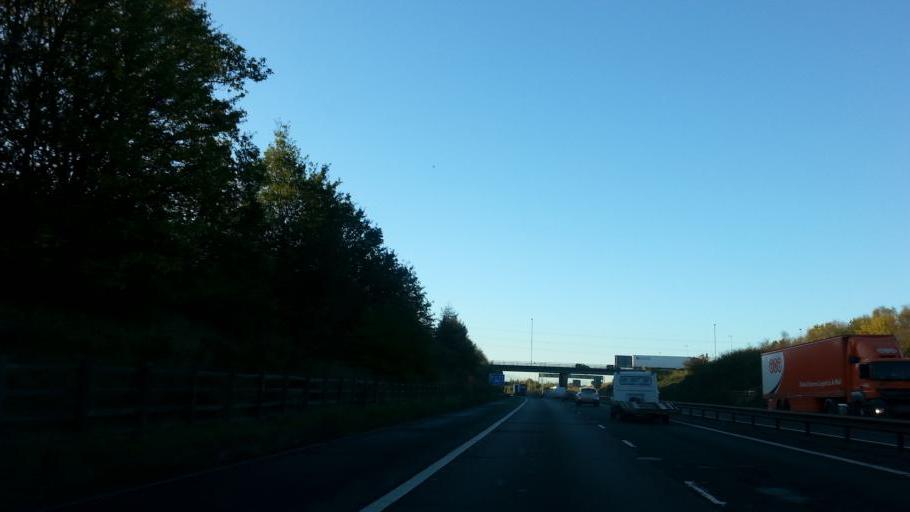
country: GB
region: England
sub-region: Warwickshire
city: Curdworth
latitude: 52.5393
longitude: -1.7258
